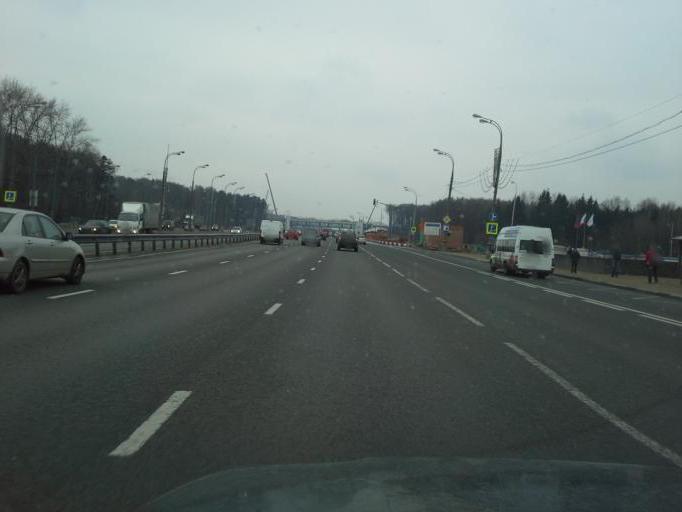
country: RU
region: Moscow
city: Troparevo
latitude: 55.6435
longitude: 37.4694
